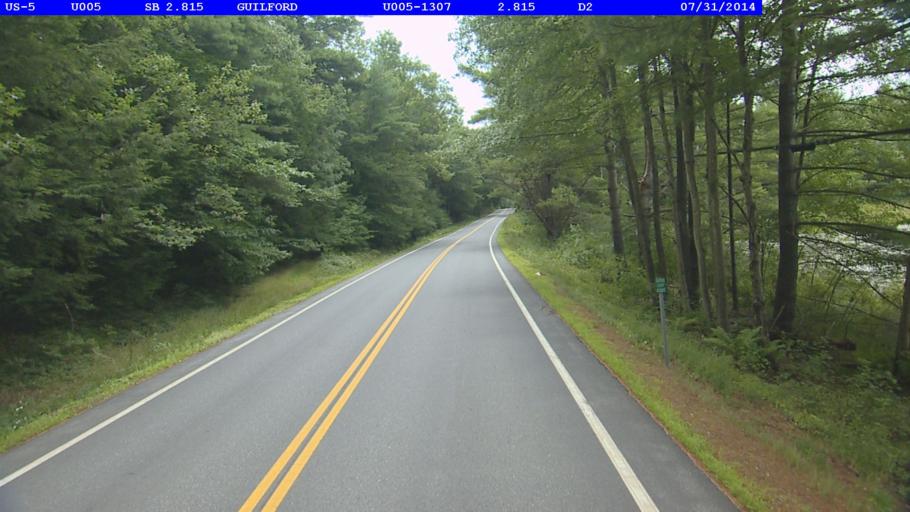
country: US
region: Vermont
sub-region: Windham County
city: Brattleboro
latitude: 42.7700
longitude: -72.5672
